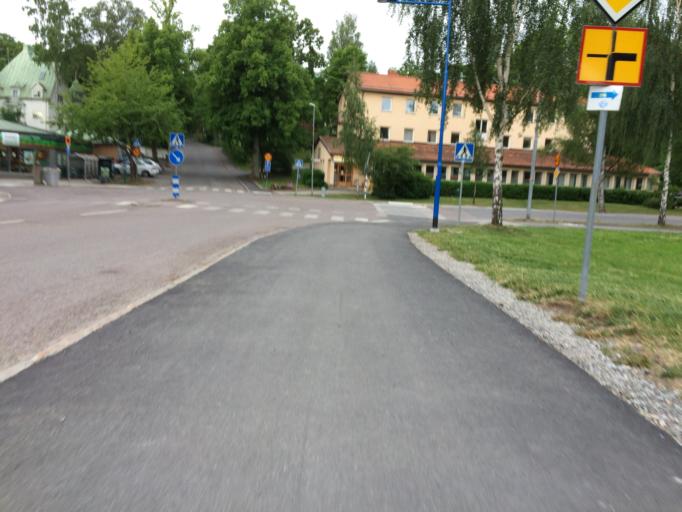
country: SE
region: Stockholm
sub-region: Danderyds Kommun
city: Djursholm
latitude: 59.3983
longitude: 18.0862
